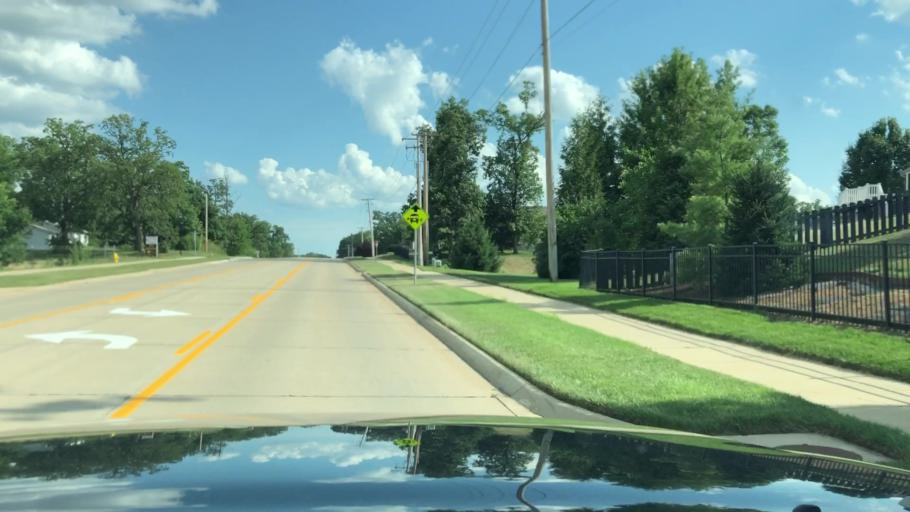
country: US
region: Missouri
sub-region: Saint Charles County
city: Wentzville
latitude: 38.8319
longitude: -90.8922
